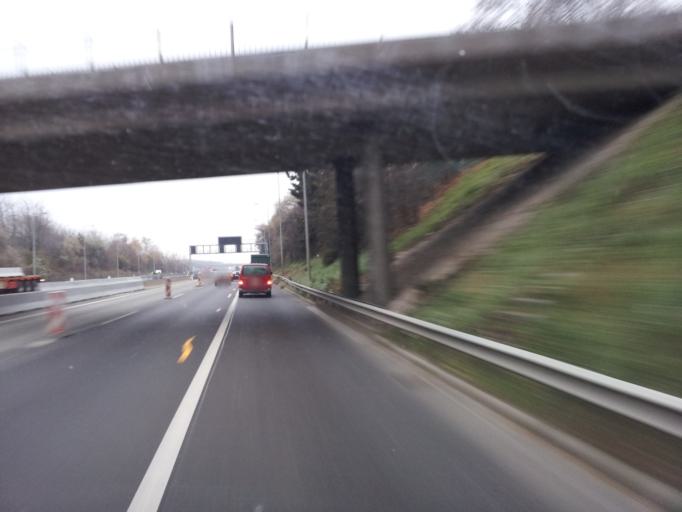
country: HU
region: Pest
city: Toeroekbalint
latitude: 47.4407
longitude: 18.9038
